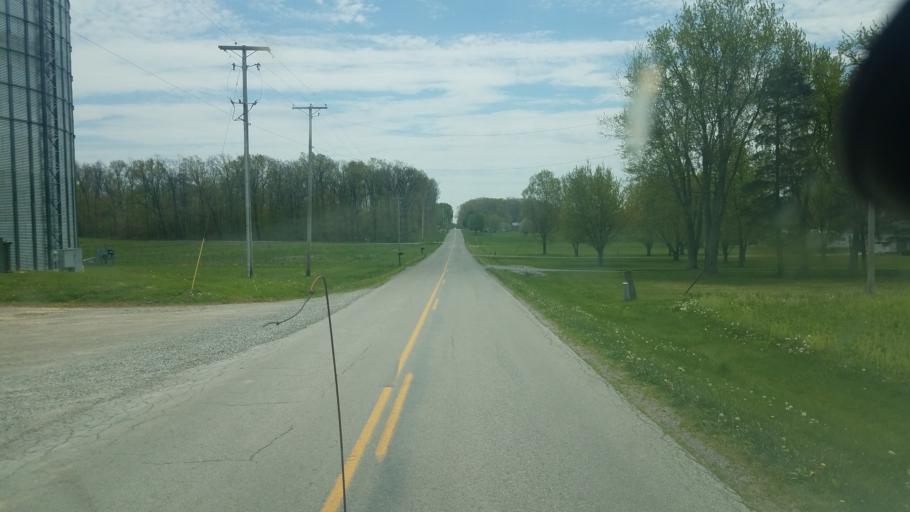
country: US
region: Ohio
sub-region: Allen County
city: Bluffton
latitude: 40.7768
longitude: -83.9672
